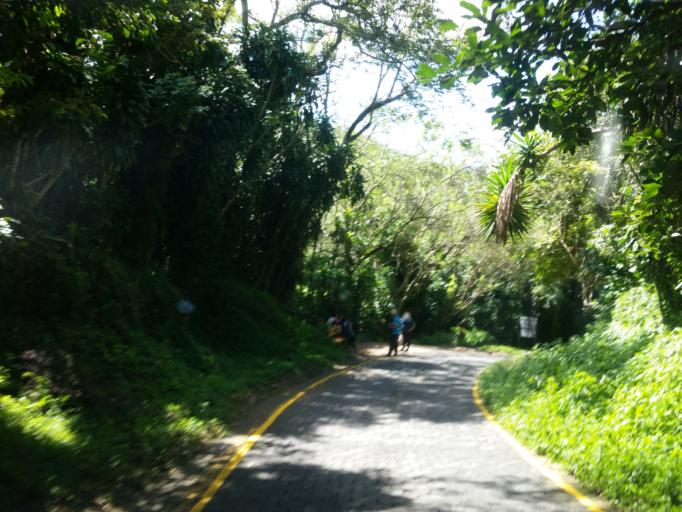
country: NI
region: Granada
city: Diriomo
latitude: 11.8400
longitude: -85.9967
